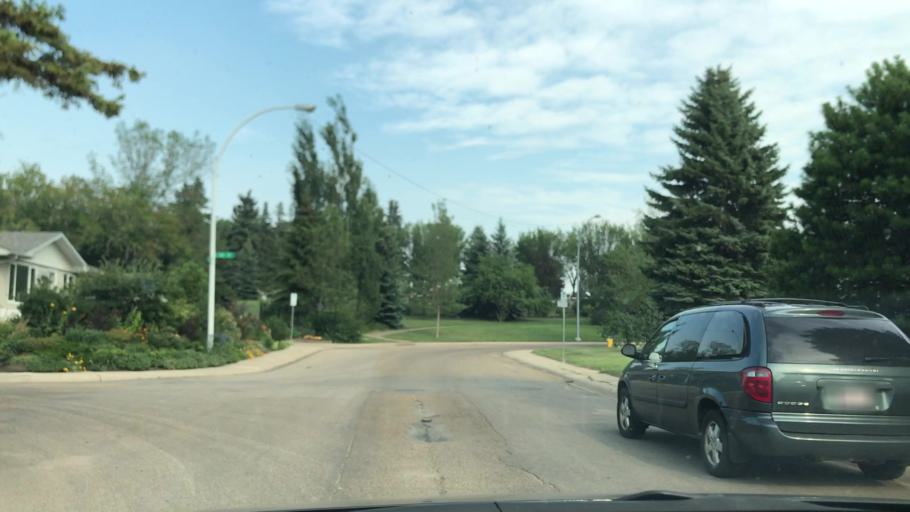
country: CA
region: Alberta
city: Edmonton
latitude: 53.4903
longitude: -113.5093
